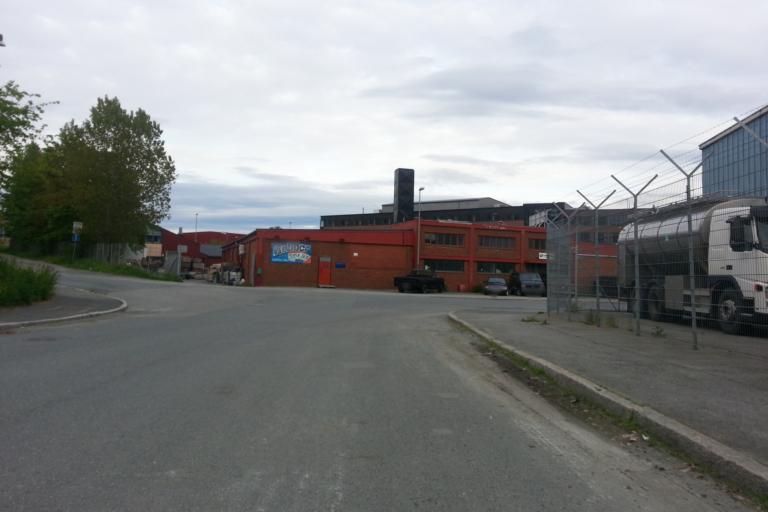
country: NO
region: Sor-Trondelag
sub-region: Trondheim
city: Trondheim
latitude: 63.4438
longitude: 10.4267
